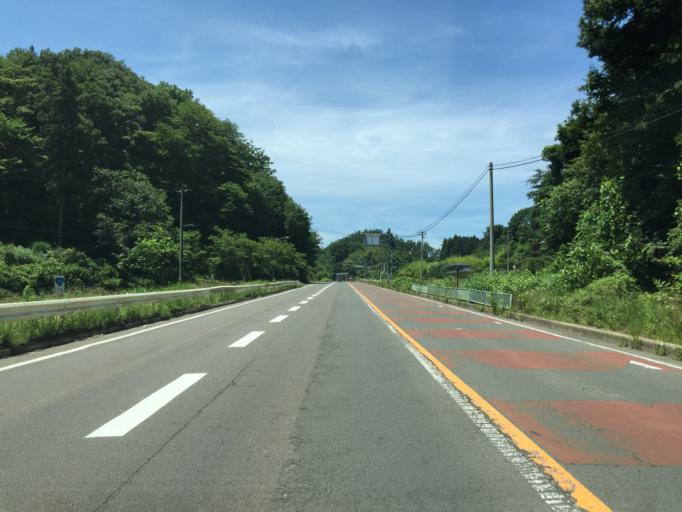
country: JP
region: Fukushima
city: Fukushima-shi
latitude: 37.7486
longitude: 140.5317
